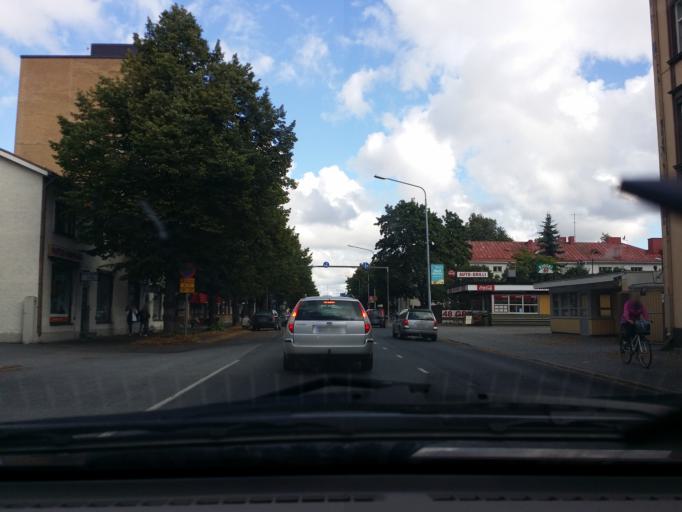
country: FI
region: Satakunta
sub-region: Pori
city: Pori
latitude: 61.4821
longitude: 21.7941
